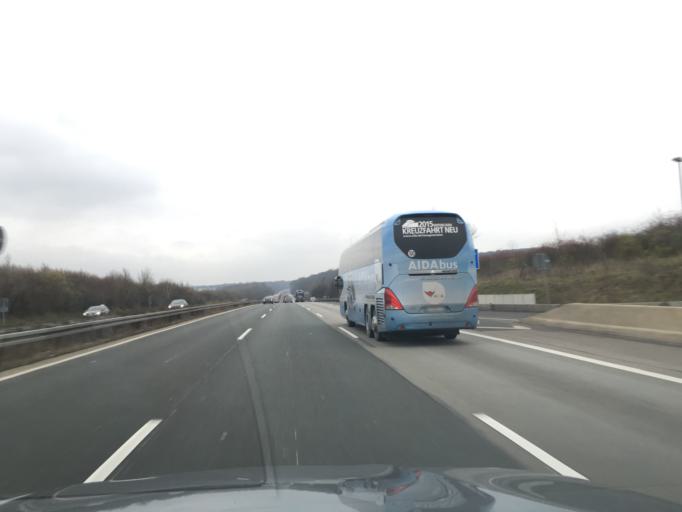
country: DE
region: Hesse
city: Eppstein
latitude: 50.0993
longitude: 8.3510
